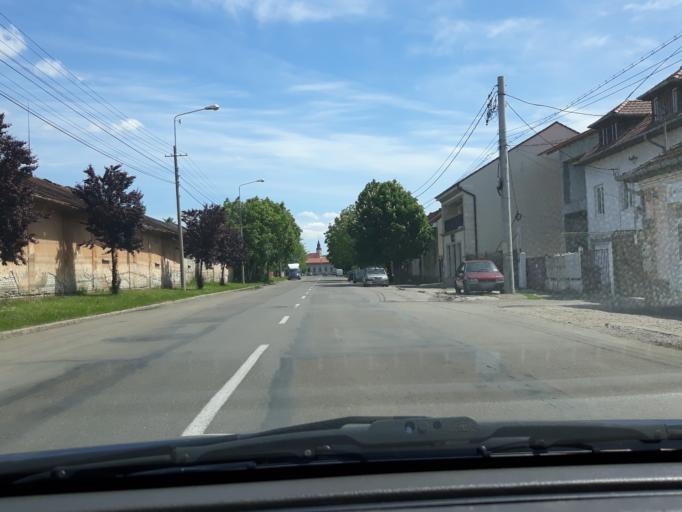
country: RO
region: Bihor
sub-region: Comuna Biharea
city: Oradea
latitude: 47.0513
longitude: 21.9144
